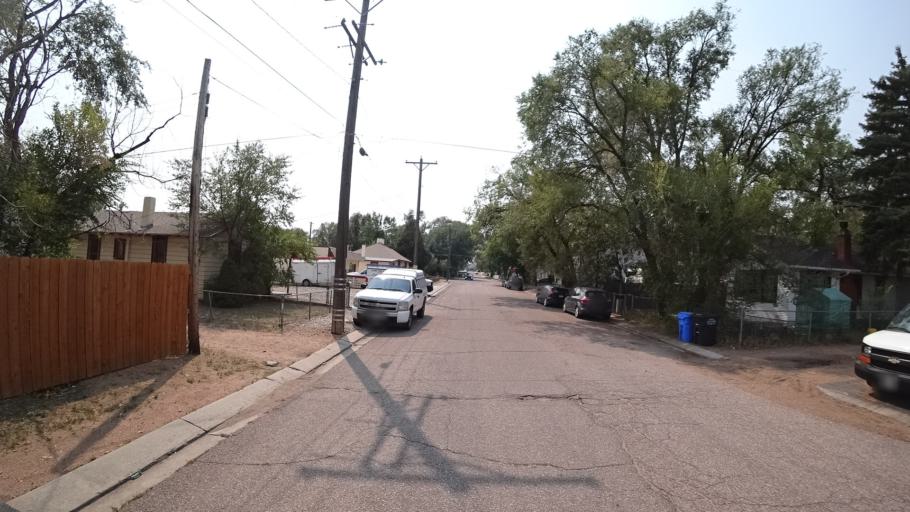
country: US
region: Colorado
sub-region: El Paso County
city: Colorado Springs
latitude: 38.8135
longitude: -104.8193
